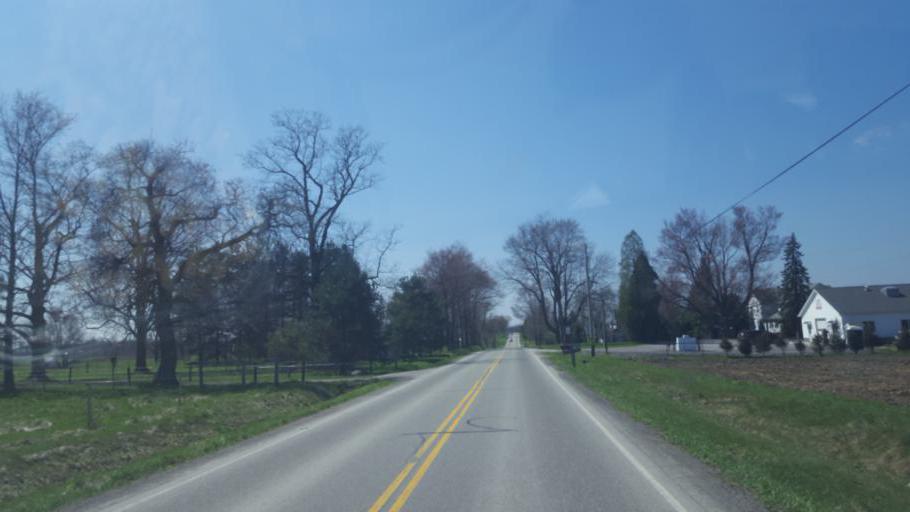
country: US
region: Ohio
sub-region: Portage County
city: Hiram
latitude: 41.3870
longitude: -81.1108
